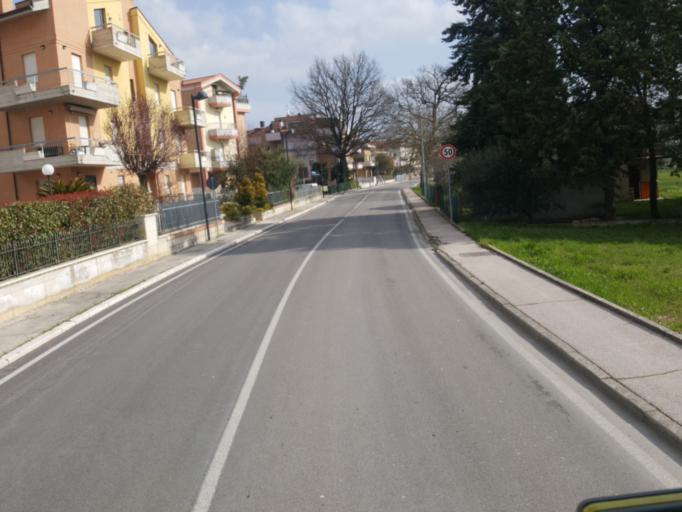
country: IT
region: The Marches
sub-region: Provincia di Macerata
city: Passo di Treia
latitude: 43.2802
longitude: 13.3235
